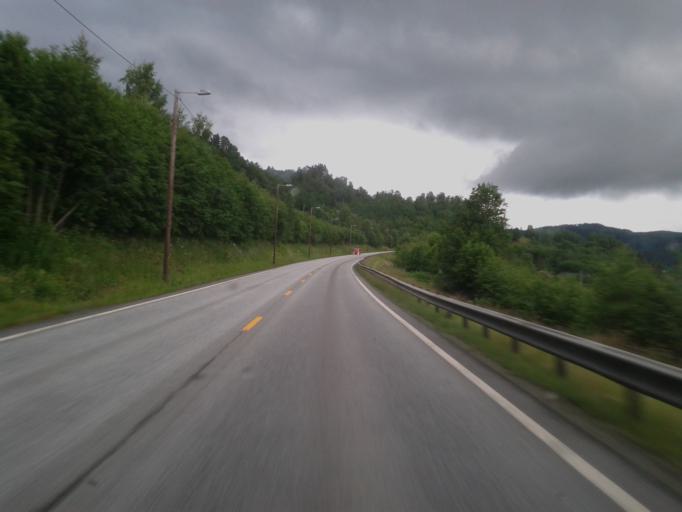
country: NO
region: Sor-Trondelag
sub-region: Melhus
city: Lundamo
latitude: 63.1171
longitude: 10.2430
